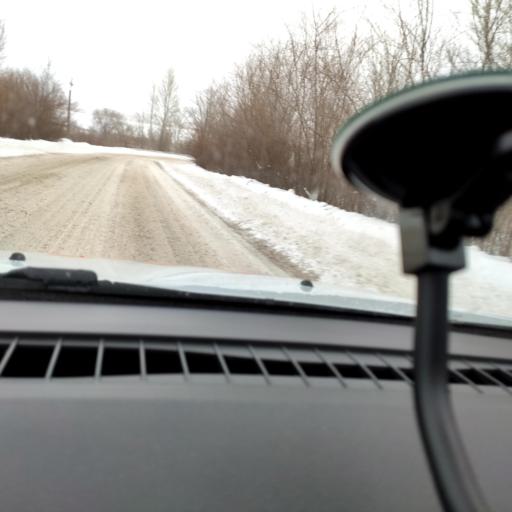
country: RU
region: Samara
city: Dubovyy Umet
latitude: 53.0404
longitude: 50.2331
